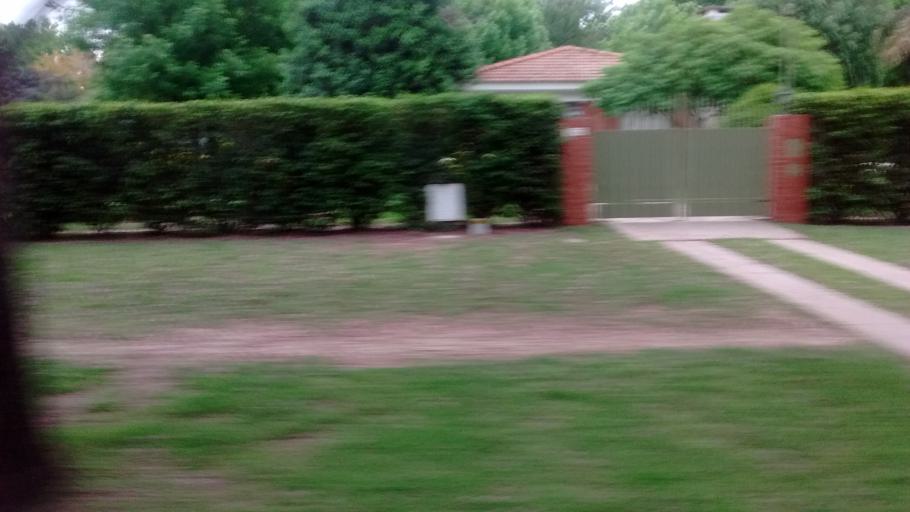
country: AR
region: Santa Fe
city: Funes
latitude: -32.9253
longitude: -60.8117
